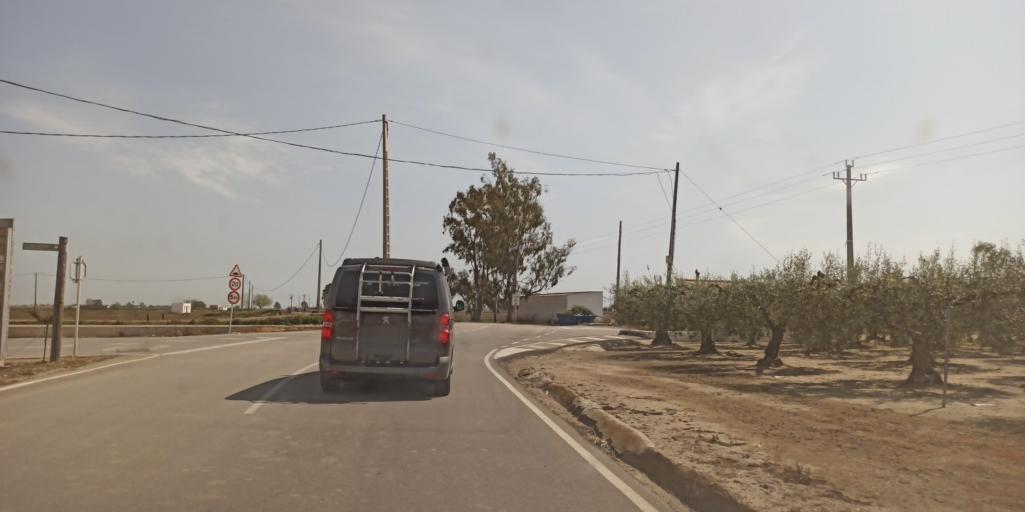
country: ES
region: Catalonia
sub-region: Provincia de Tarragona
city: Deltebre
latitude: 40.6445
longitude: 0.6887
